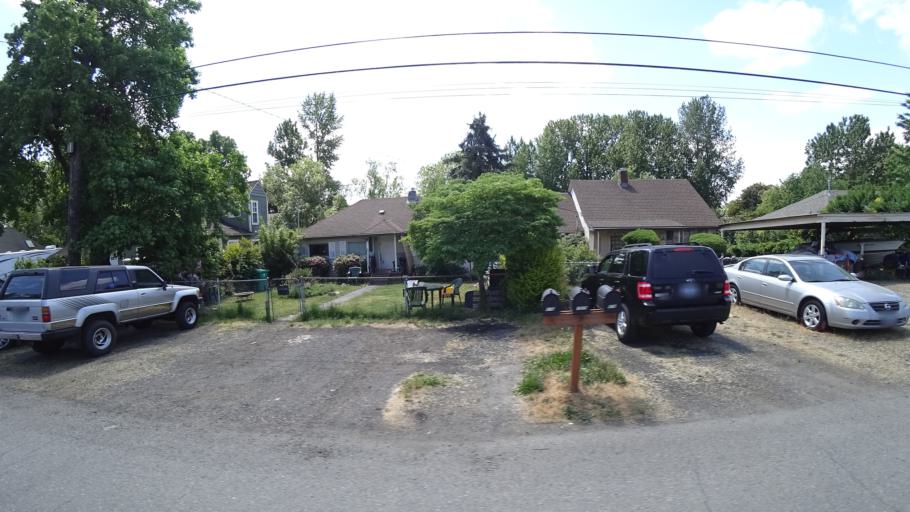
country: US
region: Washington
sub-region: Clark County
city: Vancouver
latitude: 45.5976
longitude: -122.6548
